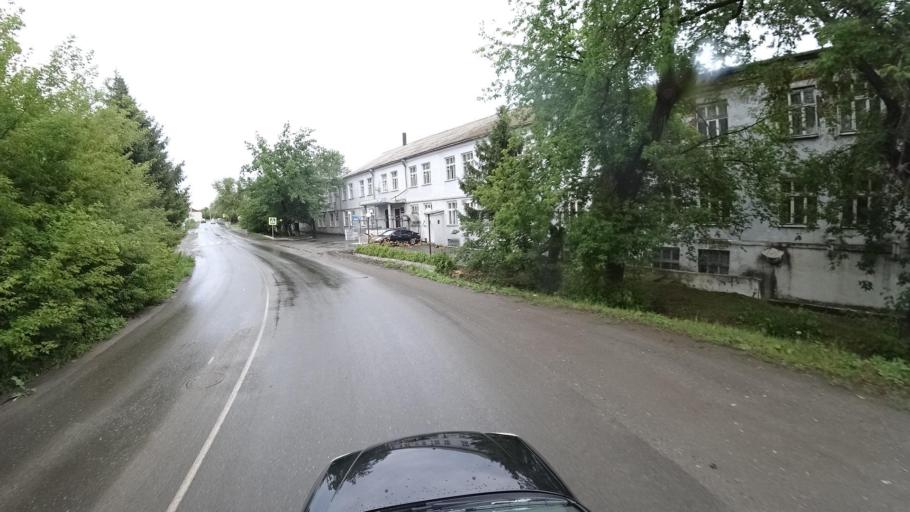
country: RU
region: Sverdlovsk
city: Kamyshlov
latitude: 56.8516
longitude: 62.7131
